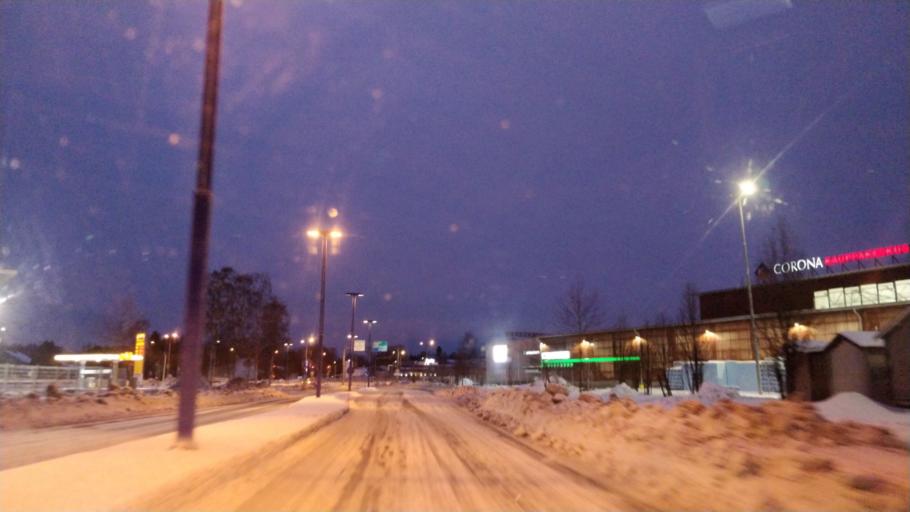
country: FI
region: Lapland
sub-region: Kemi-Tornio
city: Kemi
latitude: 65.7414
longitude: 24.5770
